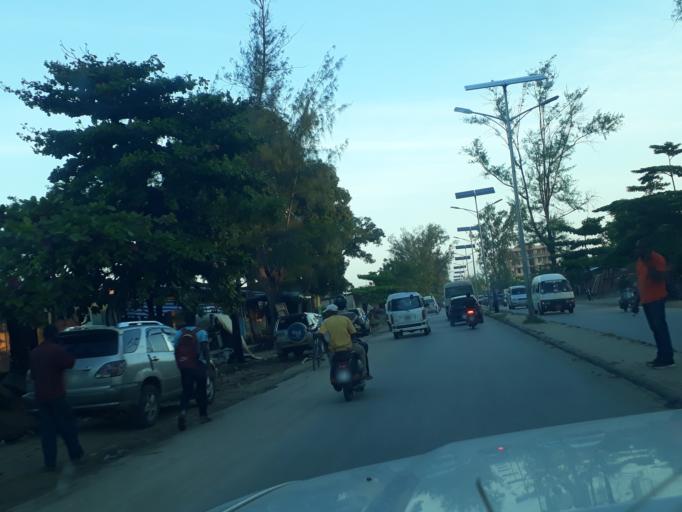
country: TZ
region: Zanzibar Urban/West
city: Zanzibar
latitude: -6.1668
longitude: 39.2262
